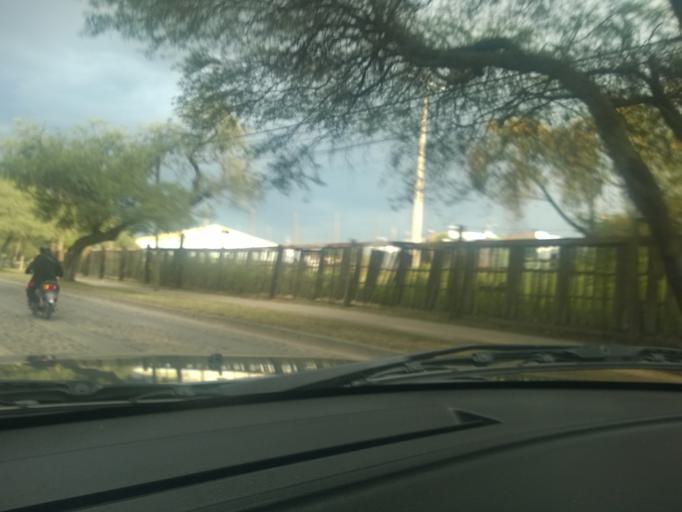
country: MX
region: Guanajuato
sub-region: Leon
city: Medina
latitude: 21.1138
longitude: -101.6217
